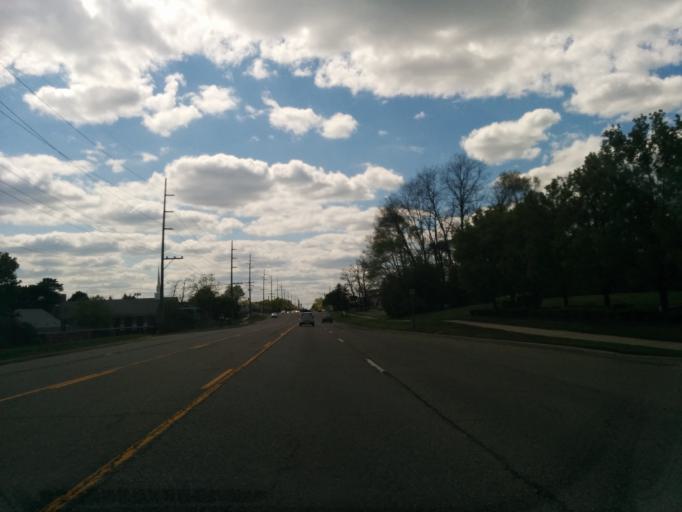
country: US
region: Michigan
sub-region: Oakland County
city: Farmington Hills
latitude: 42.4993
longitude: -83.3534
